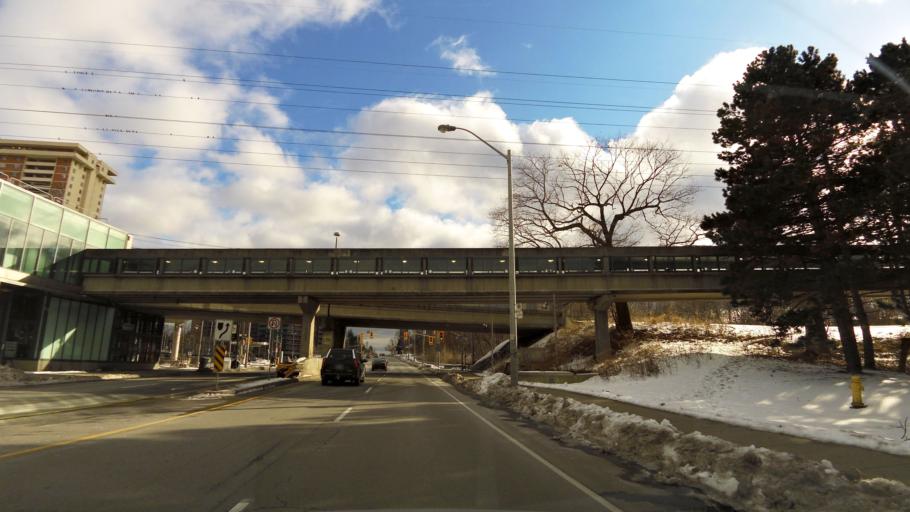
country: CA
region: Ontario
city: Scarborough
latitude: 43.6950
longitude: -79.2901
